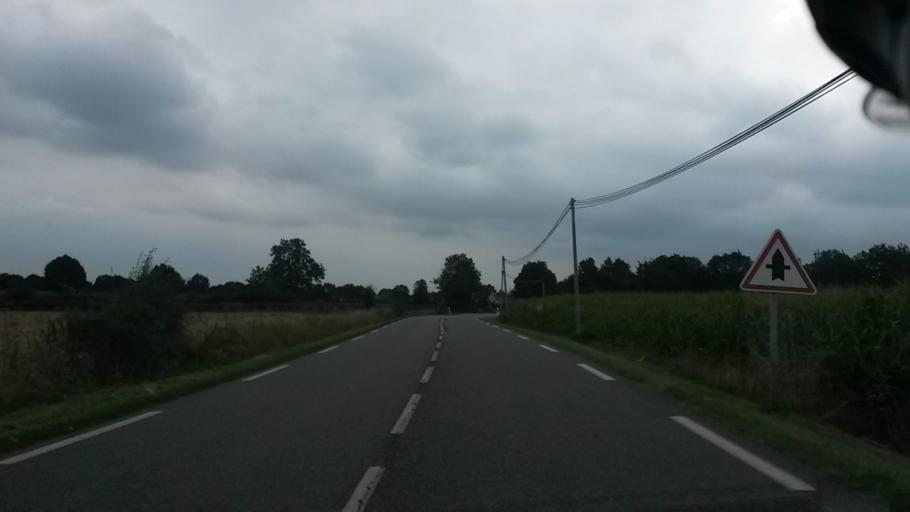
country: FR
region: Haute-Normandie
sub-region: Departement de la Seine-Maritime
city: Gaillefontaine
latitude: 49.6969
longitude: 1.6429
